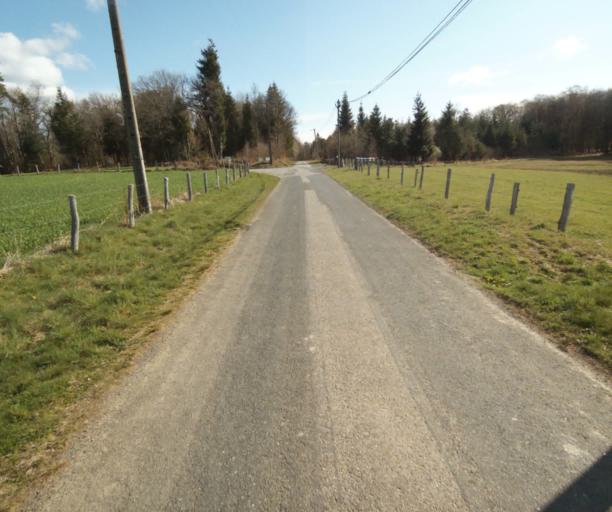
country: FR
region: Limousin
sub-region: Departement de la Correze
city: Laguenne
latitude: 45.2380
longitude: 1.9117
